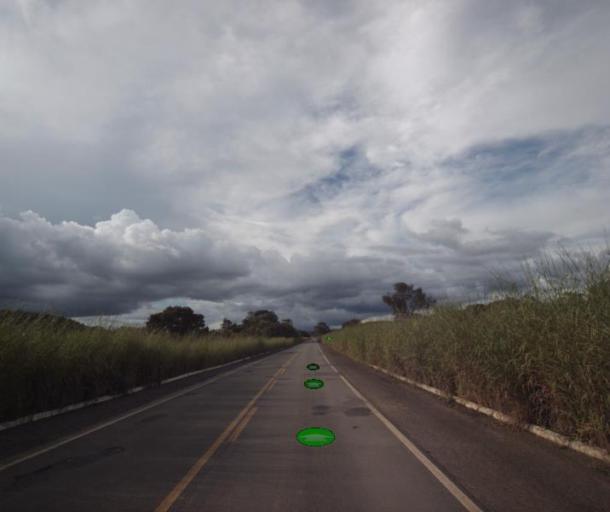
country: BR
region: Goias
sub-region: Niquelandia
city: Niquelandia
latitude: -14.6432
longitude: -48.5902
